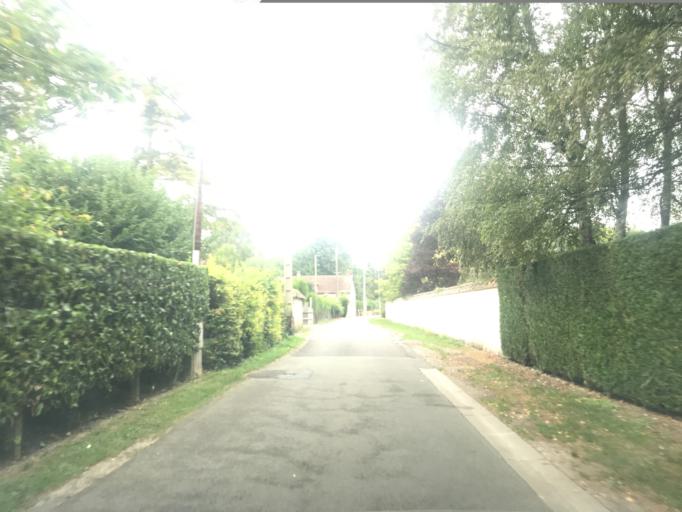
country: FR
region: Haute-Normandie
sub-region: Departement de l'Eure
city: Houlbec-Cocherel
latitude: 49.0744
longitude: 1.2855
